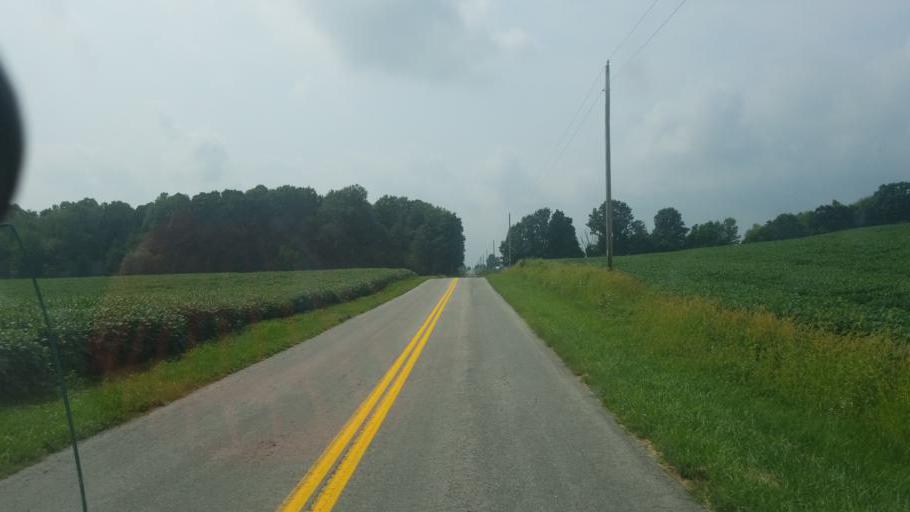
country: US
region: Ohio
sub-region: Huron County
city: Greenwich
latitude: 41.0522
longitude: -82.5529
